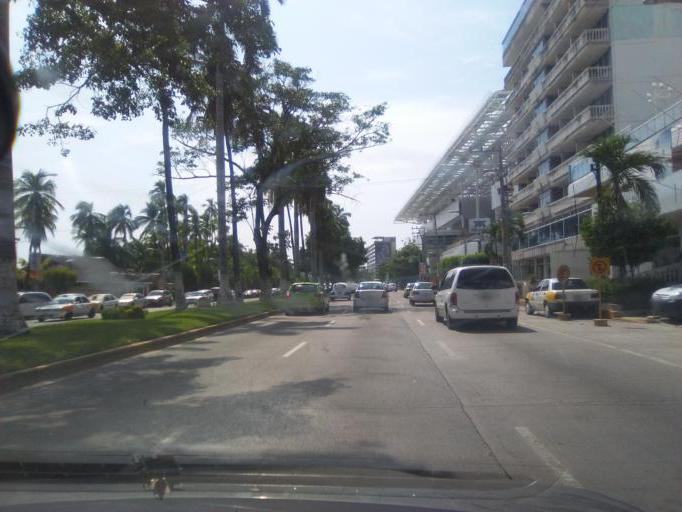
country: MX
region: Guerrero
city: Acapulco de Juarez
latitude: 16.8562
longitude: -99.8957
